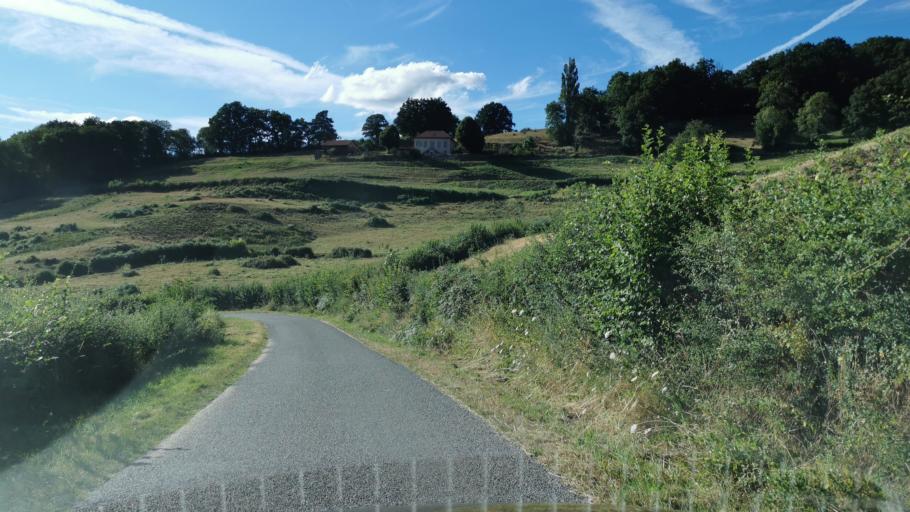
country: FR
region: Bourgogne
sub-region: Departement de Saone-et-Loire
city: Marmagne
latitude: 46.8728
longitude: 4.3358
